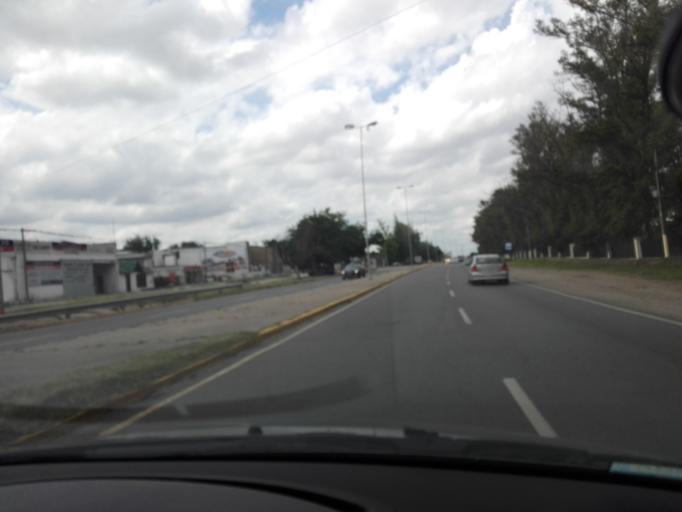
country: AR
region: Cordoba
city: Alta Gracia
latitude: -31.6499
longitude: -64.4081
